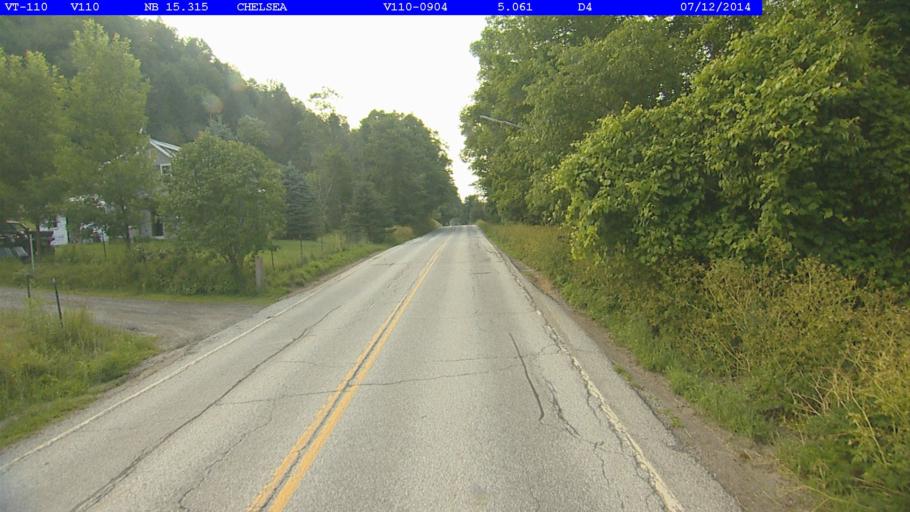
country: US
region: Vermont
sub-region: Orange County
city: Chelsea
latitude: 44.0150
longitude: -72.4641
